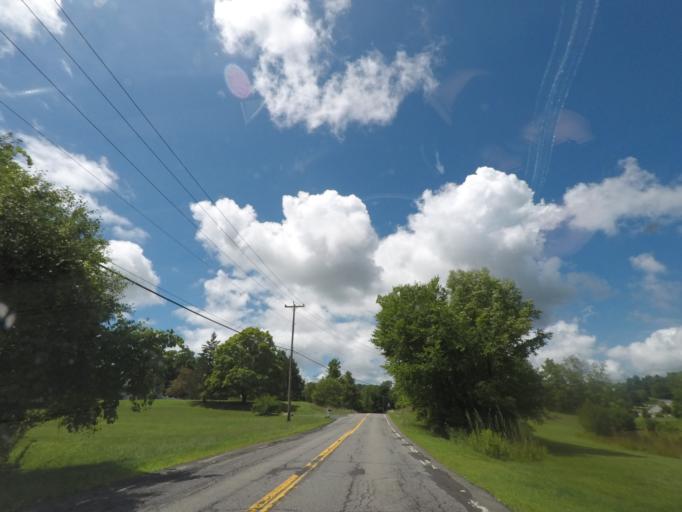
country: US
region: New York
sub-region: Rensselaer County
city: Wynantskill
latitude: 42.6679
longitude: -73.6576
